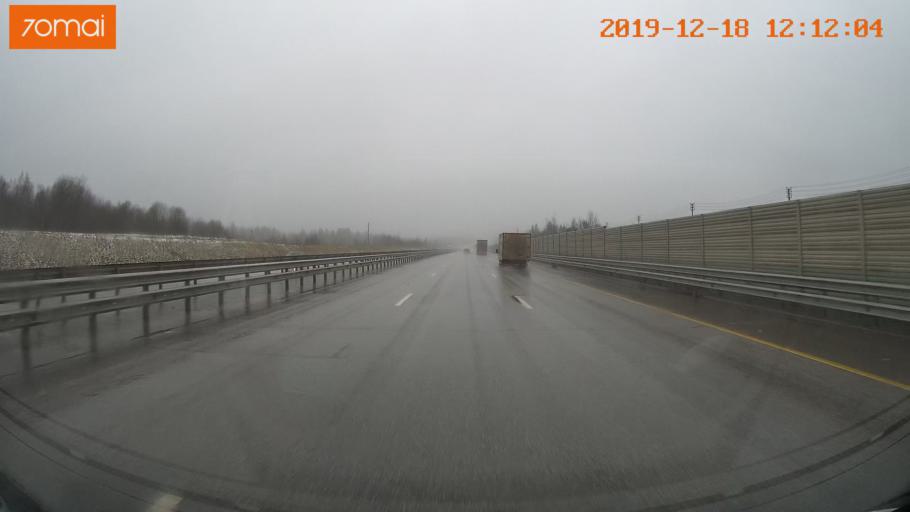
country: RU
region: Moskovskaya
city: Rumyantsevo
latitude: 55.9340
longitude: 36.5548
